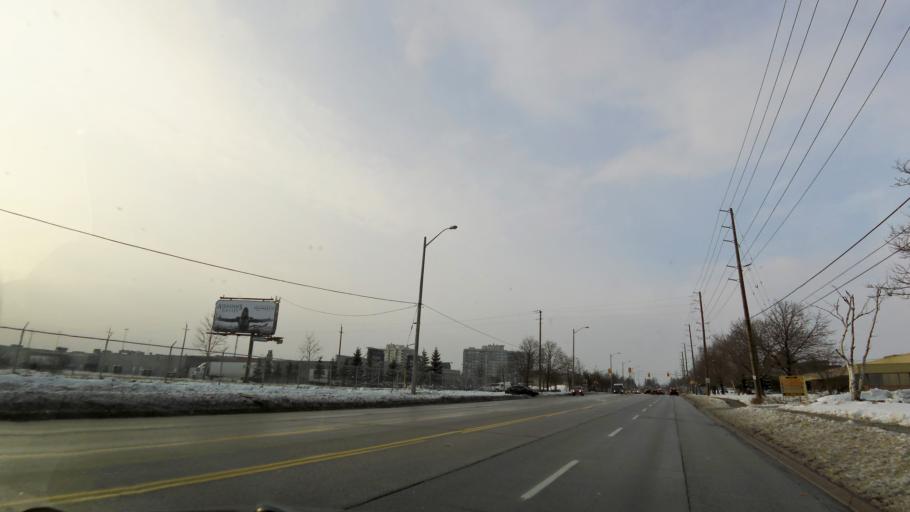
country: CA
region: Ontario
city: Brampton
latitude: 43.7071
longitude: -79.7313
